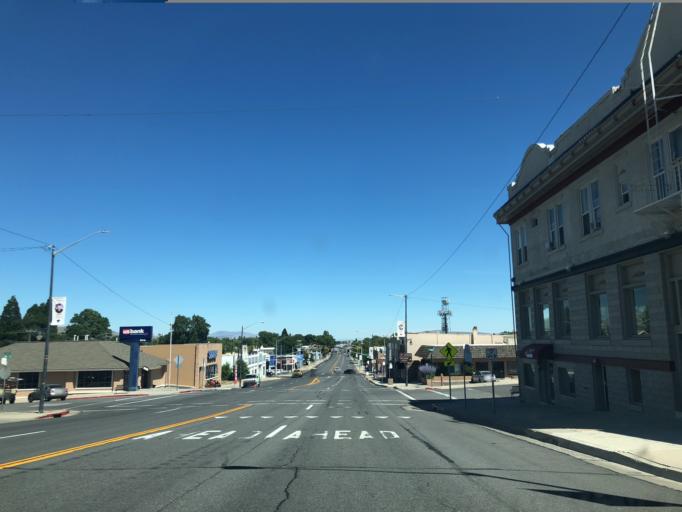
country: US
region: California
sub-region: Lassen County
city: Susanville
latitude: 40.4181
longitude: -120.6602
